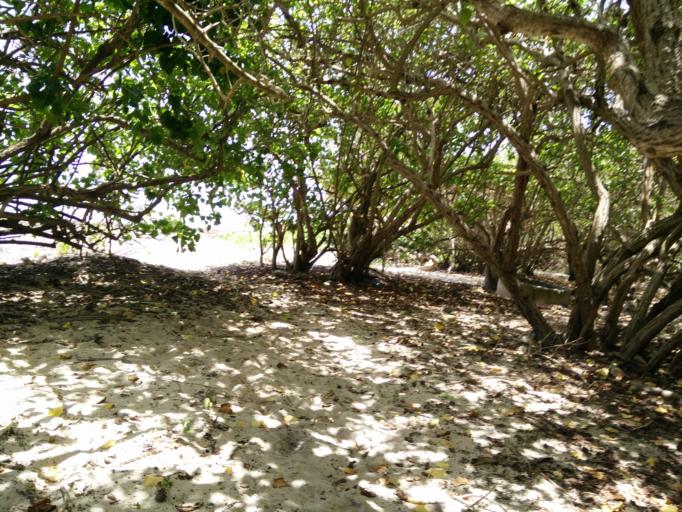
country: GP
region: Guadeloupe
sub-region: Guadeloupe
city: Sainte-Anne
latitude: 16.2396
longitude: -61.3435
